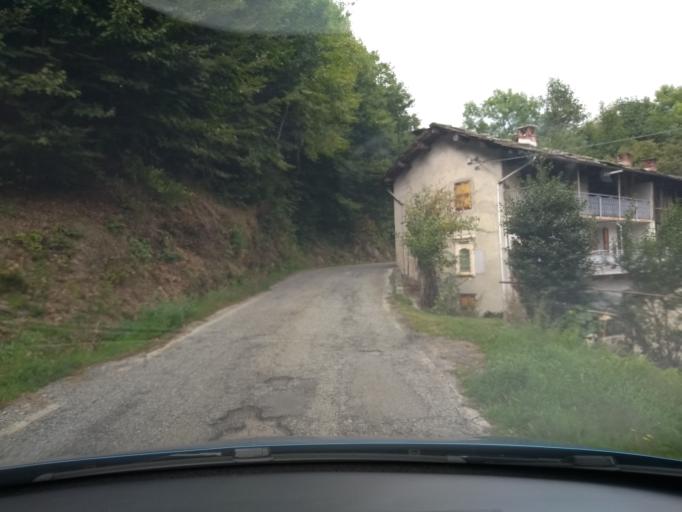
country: IT
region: Piedmont
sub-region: Provincia di Torino
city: Corio
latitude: 45.3303
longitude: 7.5160
